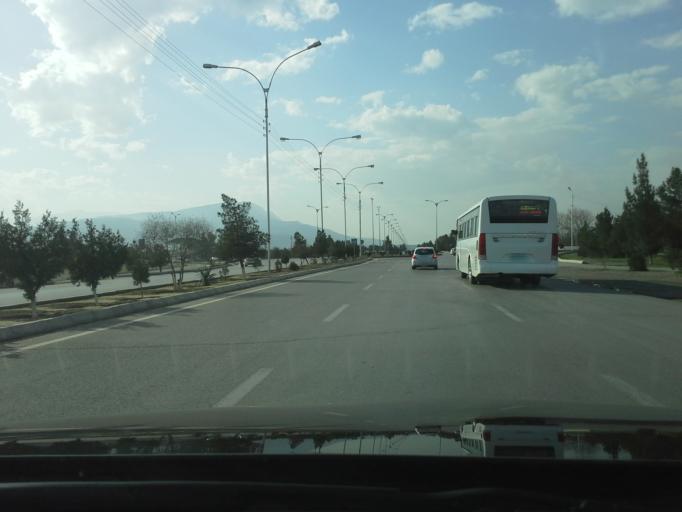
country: TM
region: Ahal
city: Abadan
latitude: 37.9765
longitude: 58.2469
